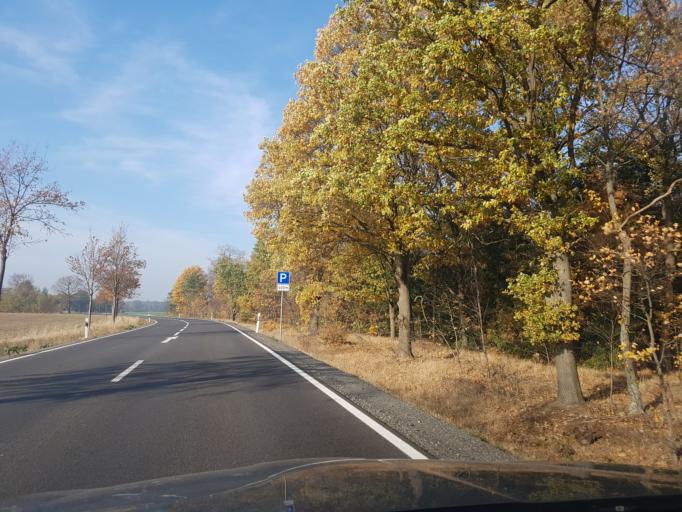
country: DE
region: Saxony
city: Arzberg
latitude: 51.5519
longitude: 13.1202
